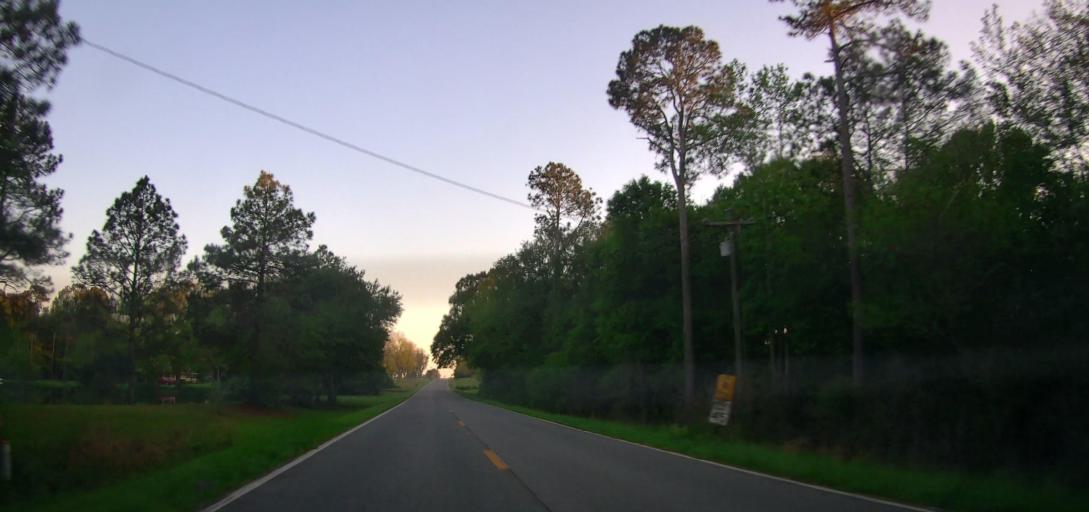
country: US
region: Georgia
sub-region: Ben Hill County
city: Fitzgerald
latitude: 31.7230
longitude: -83.3099
